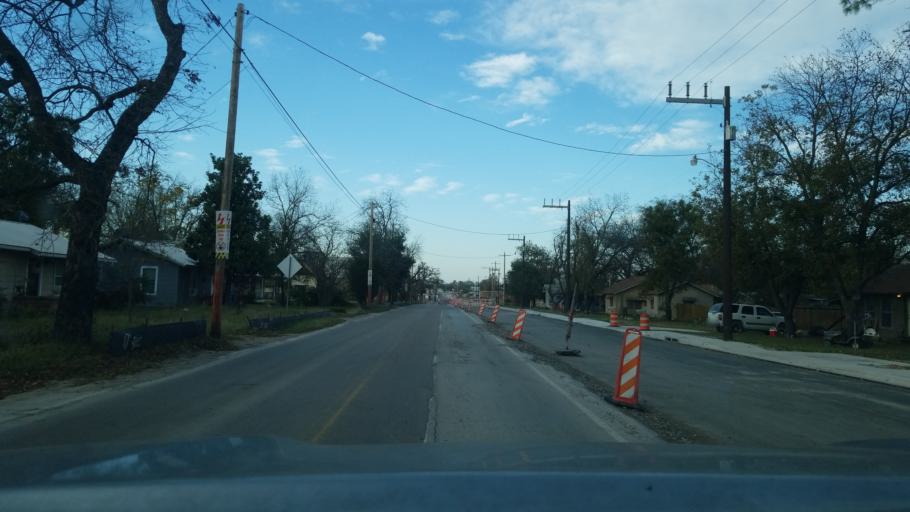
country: US
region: Texas
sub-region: Brown County
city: Lake Brownwood
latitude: 32.0926
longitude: -98.9640
